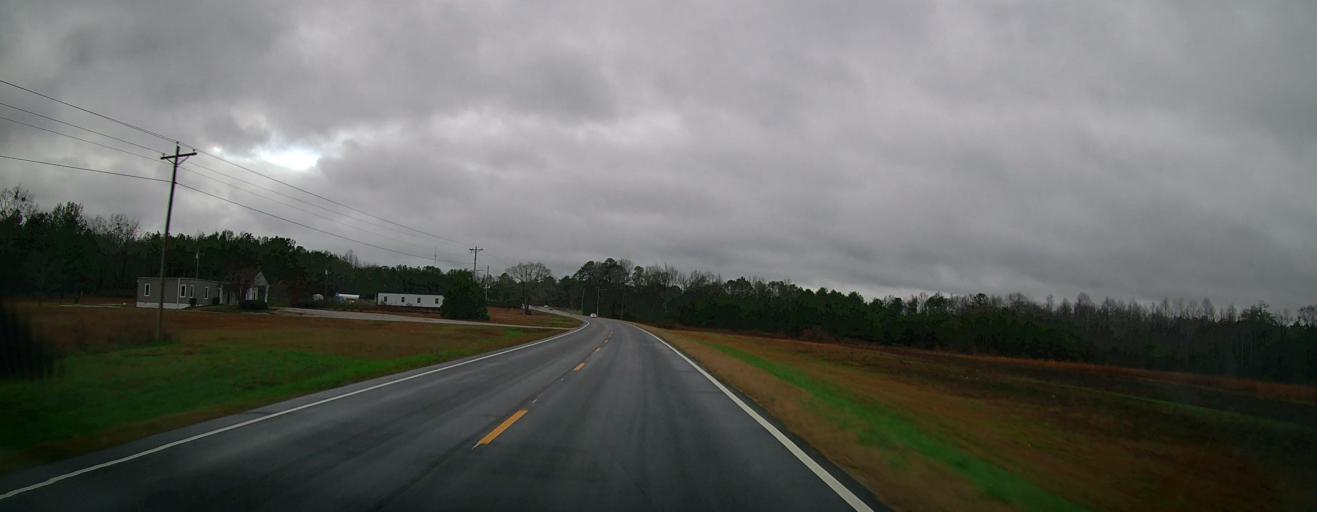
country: US
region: Alabama
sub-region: Chilton County
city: Thorsby
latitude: 32.7737
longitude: -86.8830
